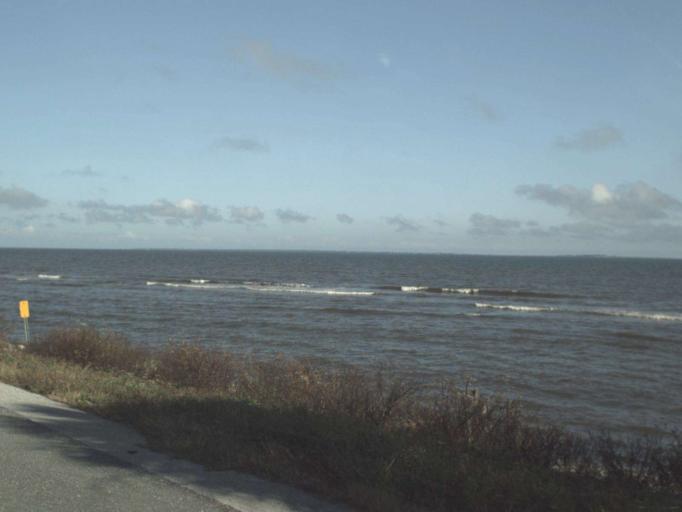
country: US
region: Florida
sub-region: Franklin County
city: Carrabelle
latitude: 29.8124
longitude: -84.7198
